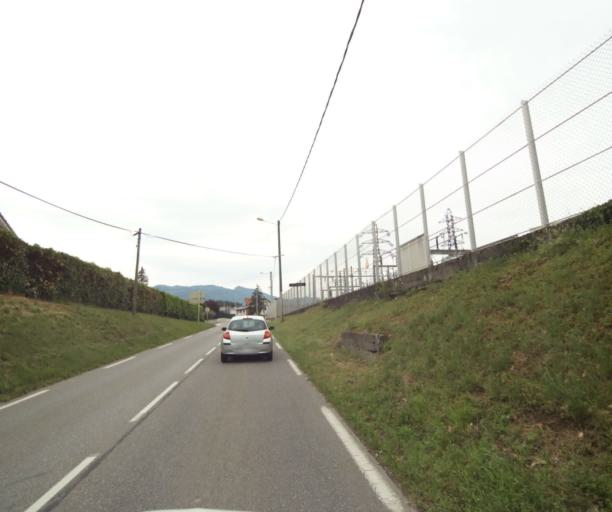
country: FR
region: Rhone-Alpes
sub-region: Departement de la Haute-Savoie
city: Thonon-les-Bains
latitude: 46.3554
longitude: 6.4760
